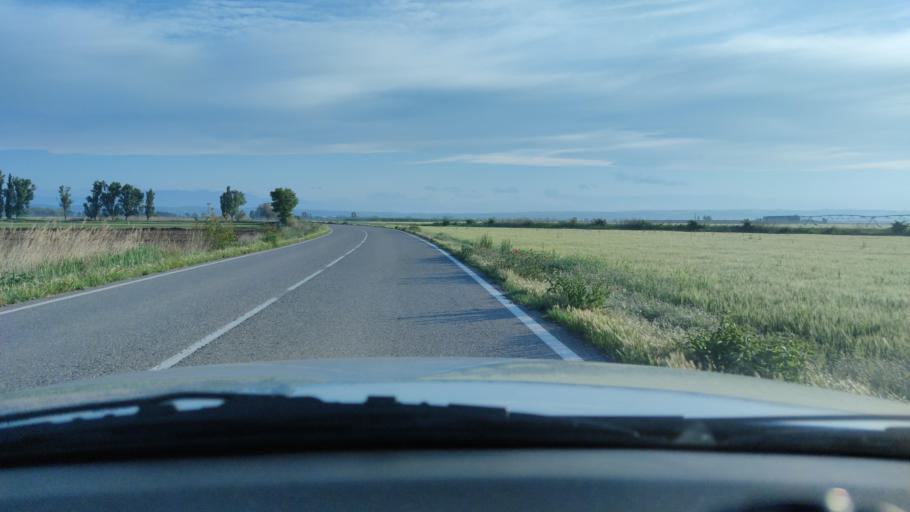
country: ES
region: Catalonia
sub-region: Provincia de Lleida
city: Ivars d'Urgell
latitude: 41.7063
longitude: 0.9826
